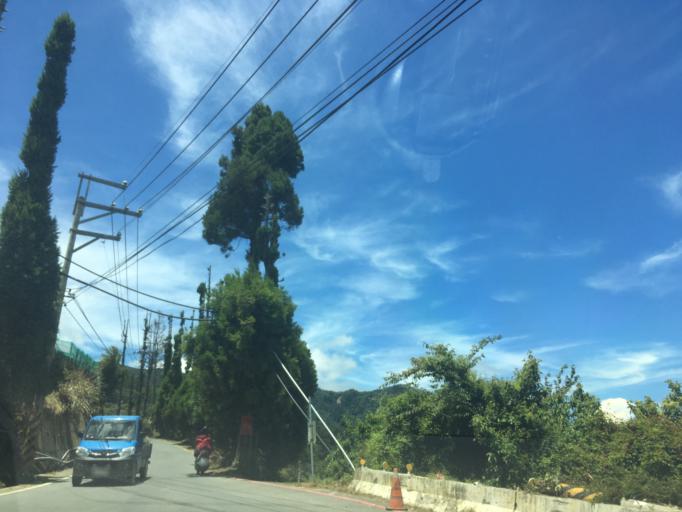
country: TW
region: Taiwan
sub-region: Nantou
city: Puli
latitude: 24.2460
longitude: 121.2420
